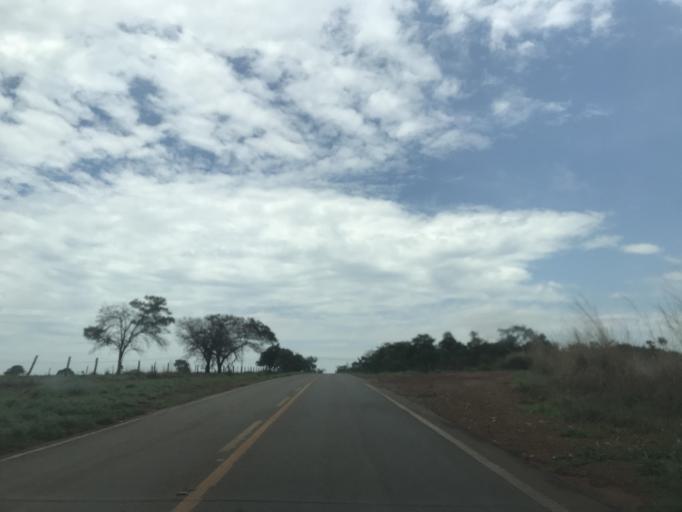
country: BR
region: Goias
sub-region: Luziania
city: Luziania
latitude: -16.2826
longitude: -47.9987
